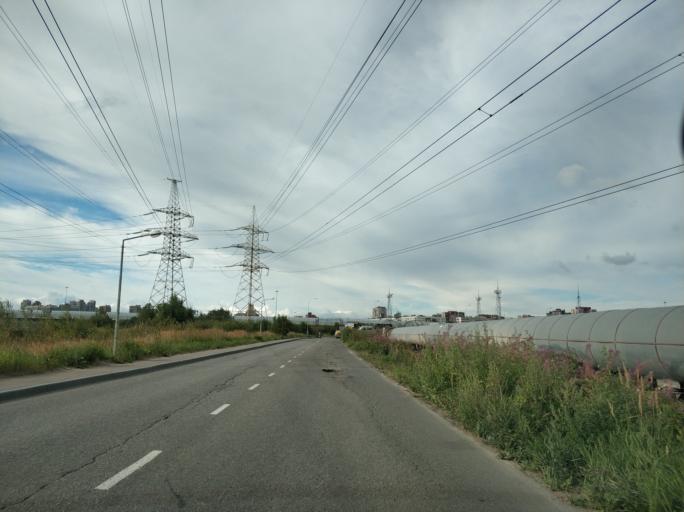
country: RU
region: Leningrad
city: Murino
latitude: 60.0468
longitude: 30.4361
